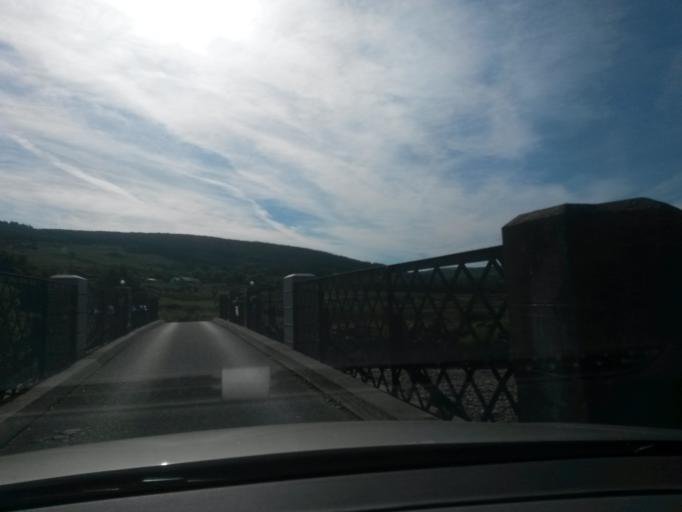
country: IE
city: Jobstown
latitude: 53.1736
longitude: -6.4208
